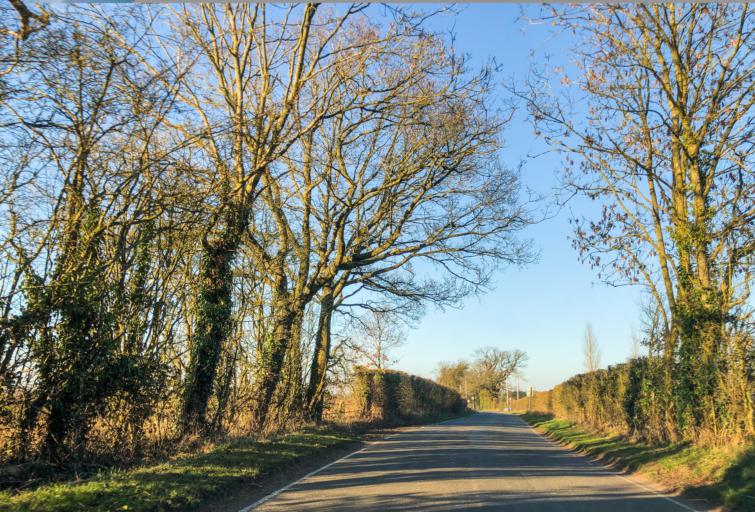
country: GB
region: England
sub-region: Warwickshire
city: Wroxall
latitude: 52.2926
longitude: -1.6600
